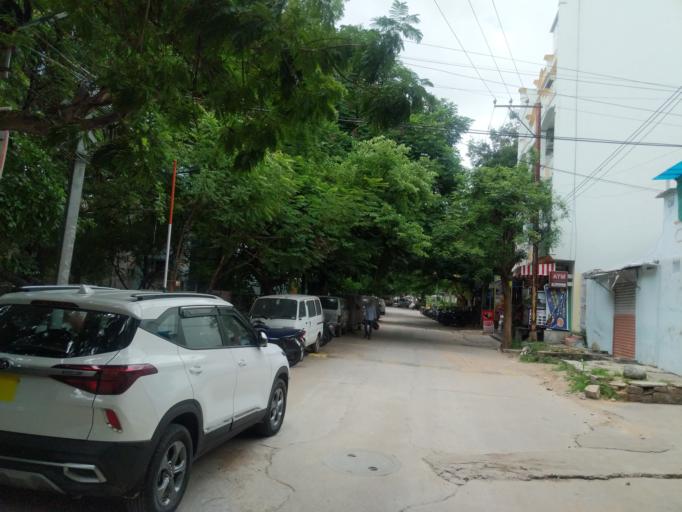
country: IN
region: Telangana
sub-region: Rangareddi
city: Kukatpalli
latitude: 17.4412
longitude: 78.4358
